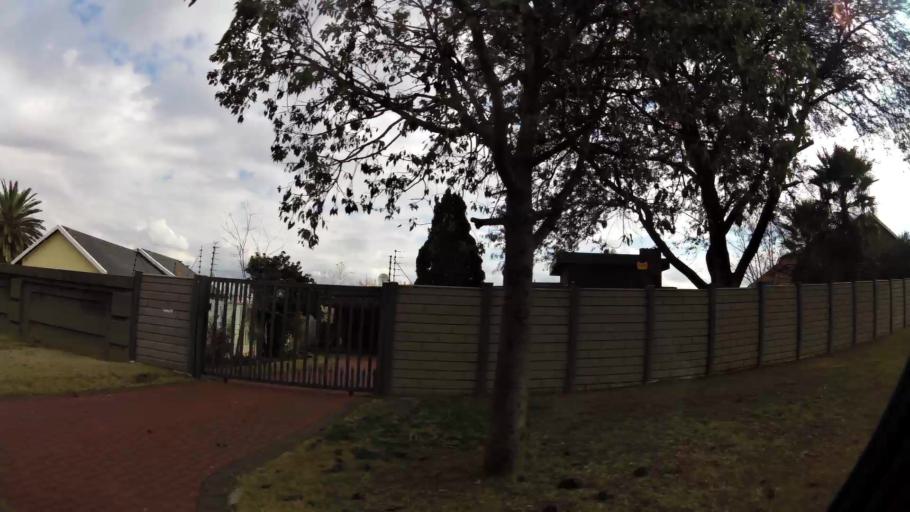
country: ZA
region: Gauteng
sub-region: Sedibeng District Municipality
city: Vanderbijlpark
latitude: -26.7065
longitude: 27.8020
